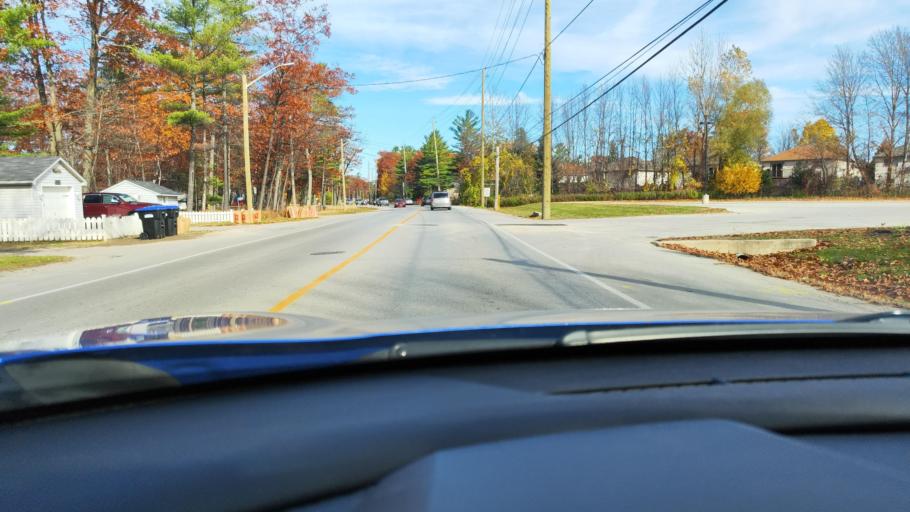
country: CA
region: Ontario
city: Wasaga Beach
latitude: 44.5120
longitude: -80.0252
